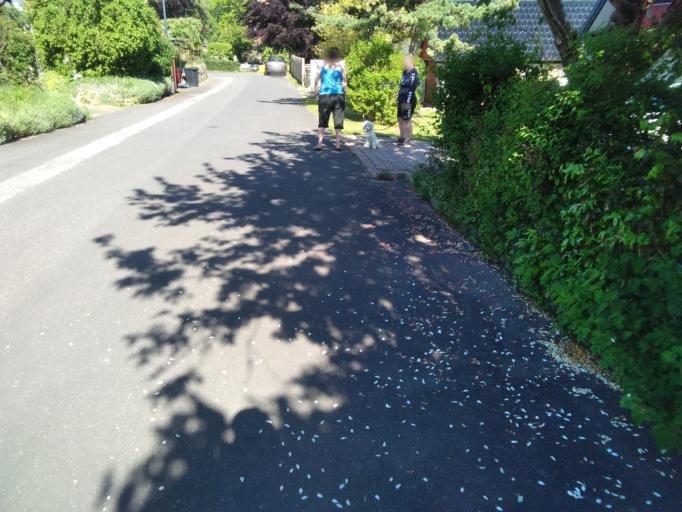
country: DK
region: Capital Region
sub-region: Egedal Kommune
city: Vekso
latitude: 55.7704
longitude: 12.2316
